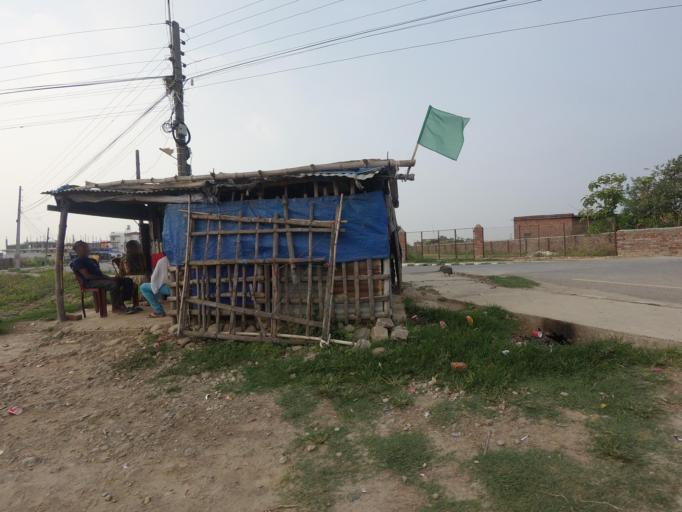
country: NP
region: Western Region
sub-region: Lumbini Zone
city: Bhairahawa
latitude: 27.5035
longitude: 83.4436
